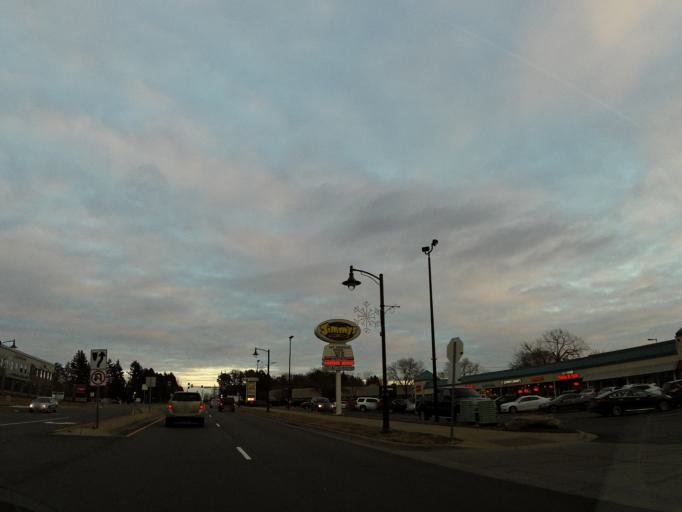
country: US
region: Minnesota
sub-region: Ramsey County
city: Vadnais Heights
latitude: 45.0503
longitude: -93.0536
